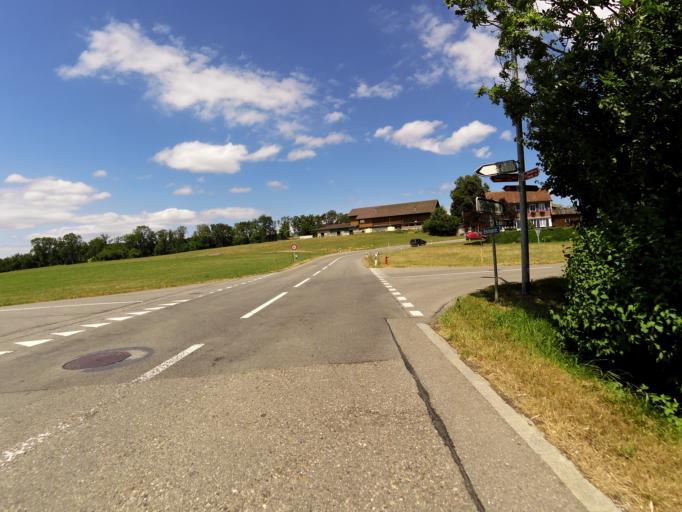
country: CH
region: Thurgau
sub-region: Weinfelden District
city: Maerstetten-Dorf
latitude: 47.6170
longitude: 9.0635
